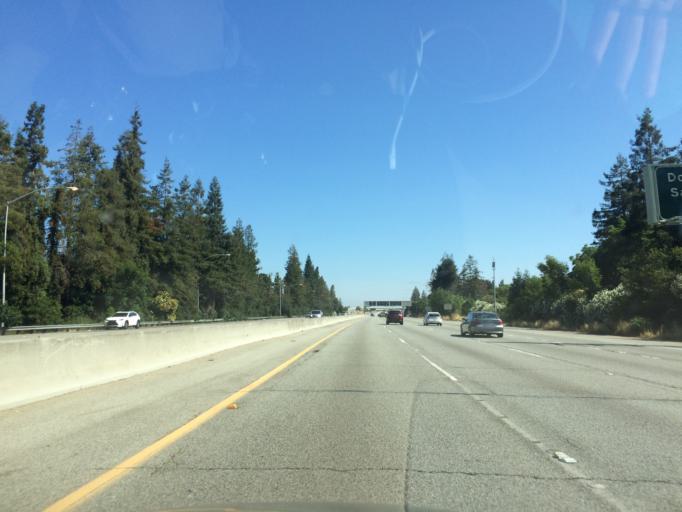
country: US
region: California
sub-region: Santa Clara County
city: Burbank
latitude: 37.3078
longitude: -121.9405
